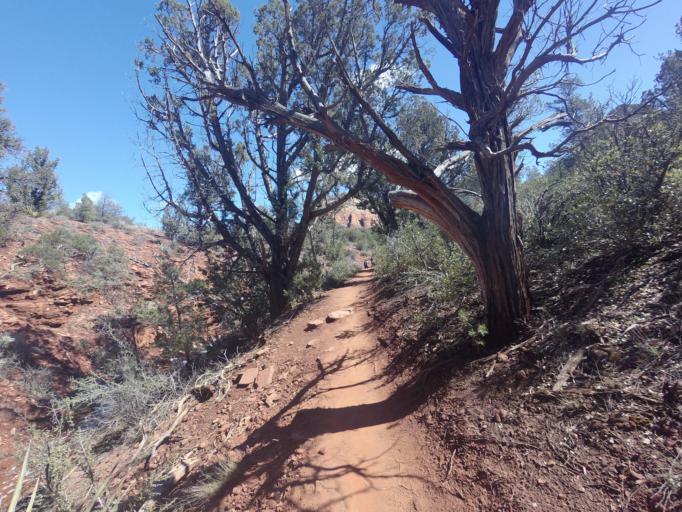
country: US
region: Arizona
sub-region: Yavapai County
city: West Sedona
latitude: 34.9012
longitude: -111.8214
